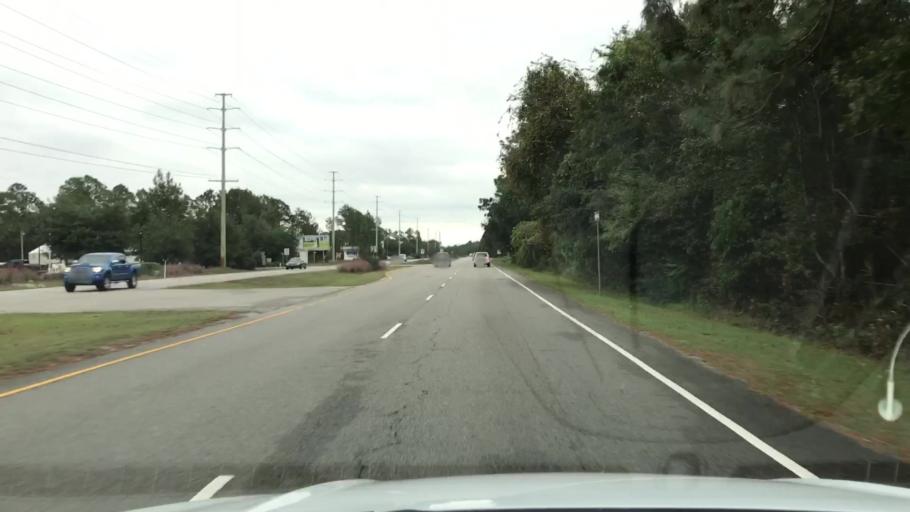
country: US
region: South Carolina
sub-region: Georgetown County
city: Georgetown
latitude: 33.4244
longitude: -79.1616
